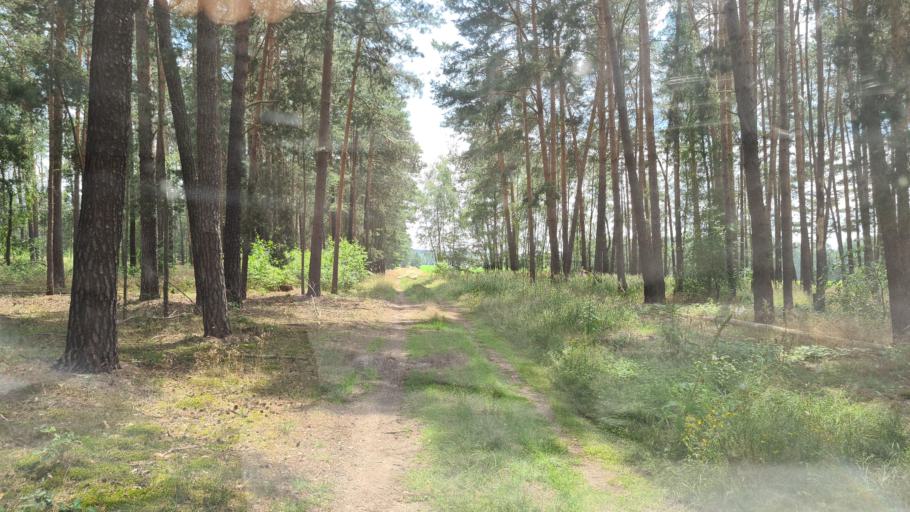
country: DE
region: Brandenburg
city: Bronkow
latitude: 51.7121
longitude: 13.8764
